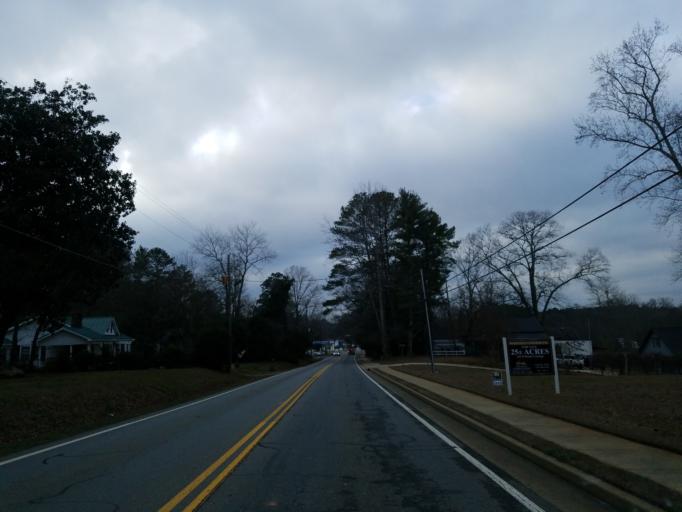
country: US
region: Georgia
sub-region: Cherokee County
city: Canton
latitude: 34.3136
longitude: -84.5474
